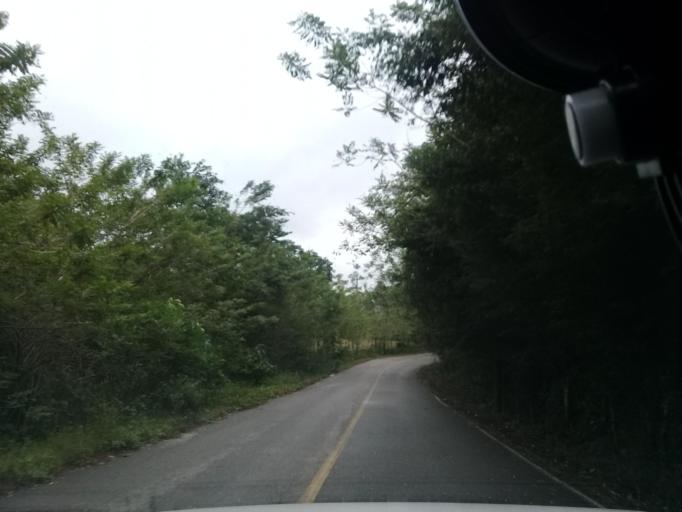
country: MX
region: Veracruz
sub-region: Chalma
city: San Pedro Coyutla
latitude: 21.2095
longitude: -98.4122
